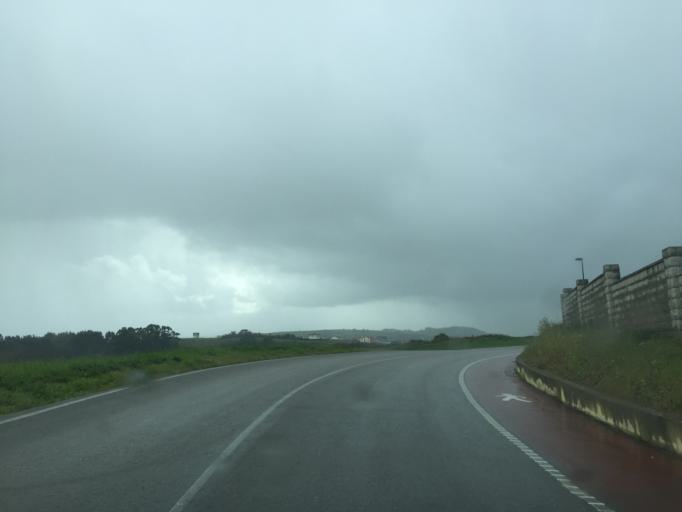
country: ES
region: Cantabria
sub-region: Provincia de Cantabria
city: Suances
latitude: 43.4279
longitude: -4.0655
